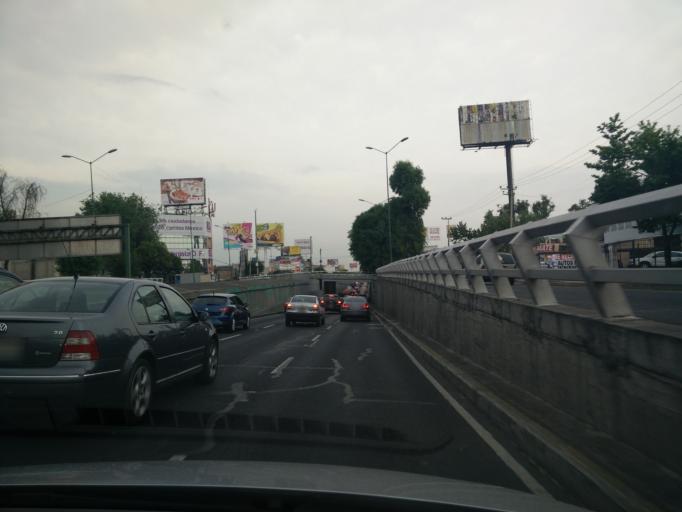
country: MX
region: Mexico City
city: Mexico City
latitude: 19.4040
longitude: -99.1269
